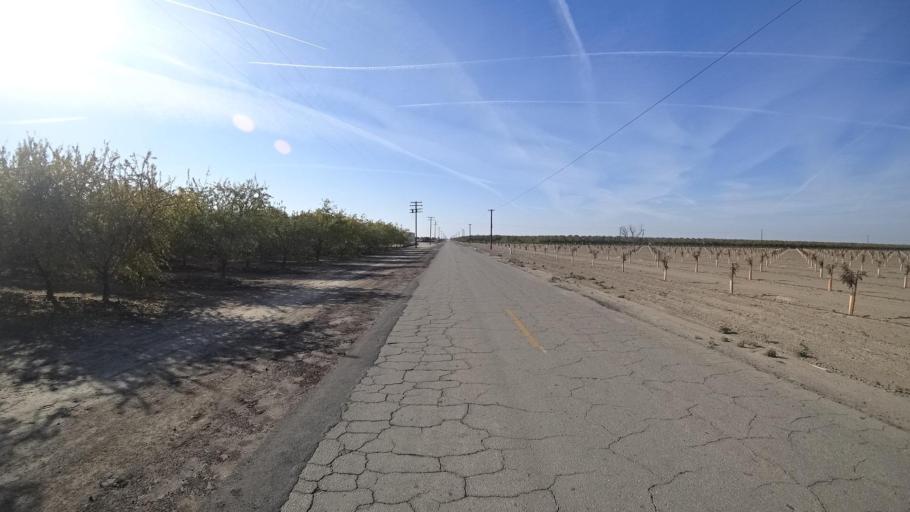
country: US
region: California
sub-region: Kern County
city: Wasco
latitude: 35.7031
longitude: -119.3641
